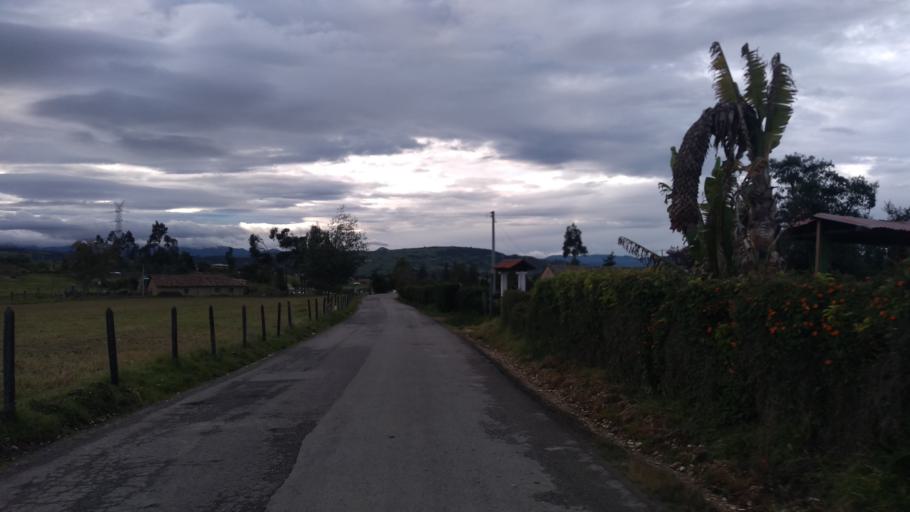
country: CO
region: Boyaca
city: Toca
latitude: 5.5805
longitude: -73.1839
